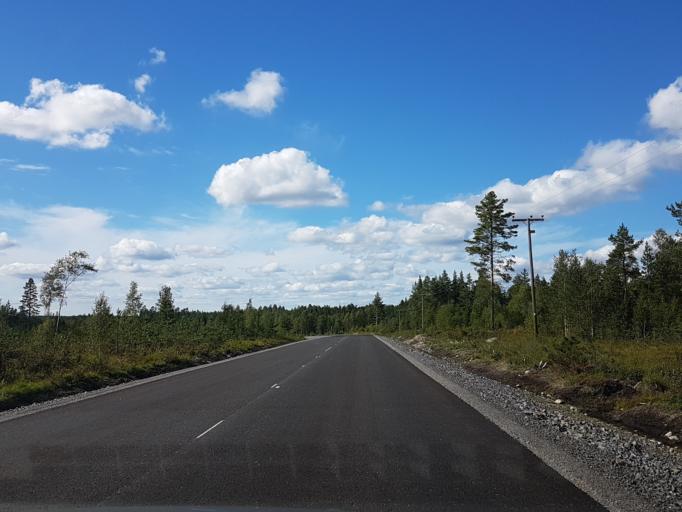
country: SE
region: Vaesterbotten
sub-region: Robertsfors Kommun
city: Robertsfors
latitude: 64.1272
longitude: 20.6605
